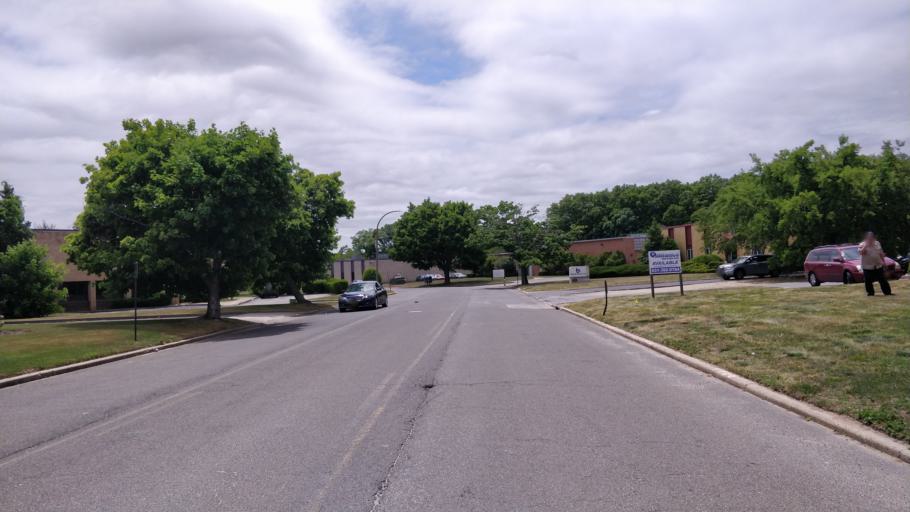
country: US
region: New York
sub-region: Suffolk County
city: Brentwood
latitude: 40.8077
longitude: -73.2745
